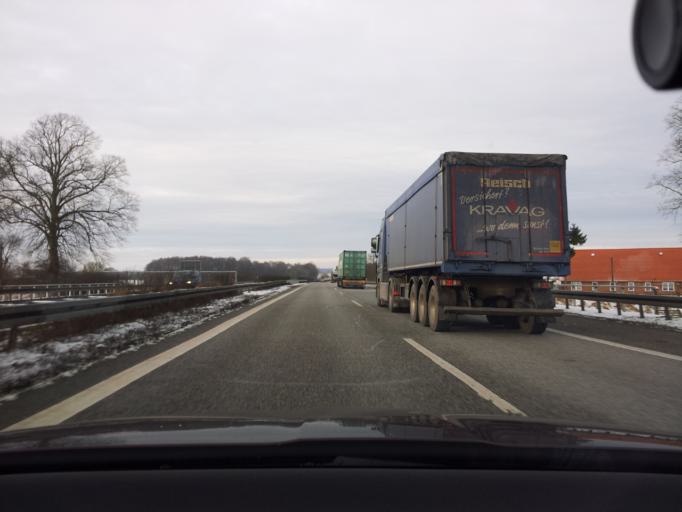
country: DE
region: Mecklenburg-Vorpommern
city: Wittenburg
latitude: 53.4989
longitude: 11.0733
